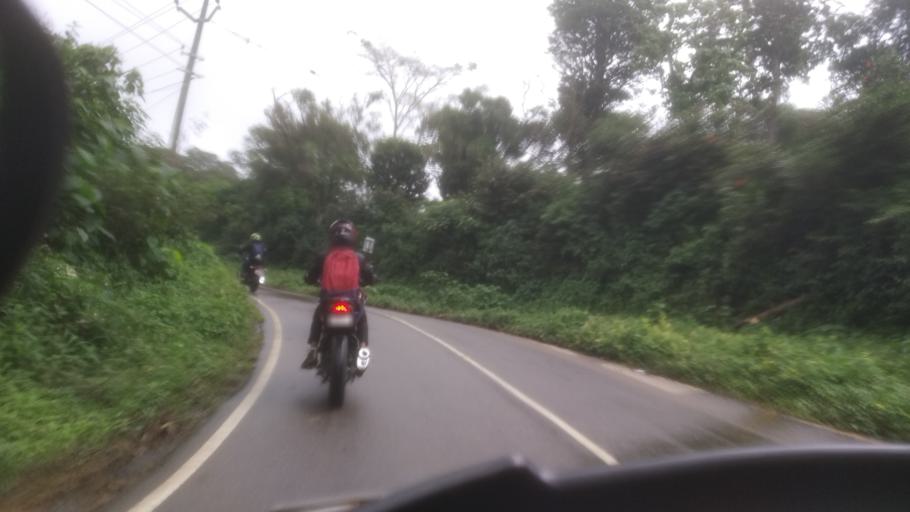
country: IN
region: Tamil Nadu
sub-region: Theni
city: Kombai
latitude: 9.8930
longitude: 77.2006
